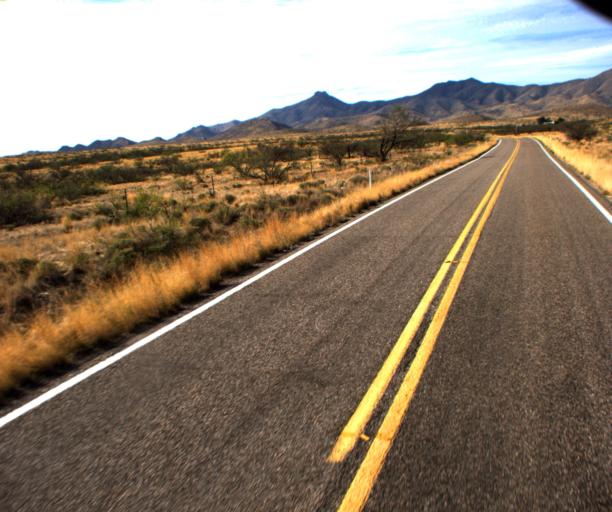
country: US
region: Arizona
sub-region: Cochise County
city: Willcox
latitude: 32.1237
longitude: -109.5559
